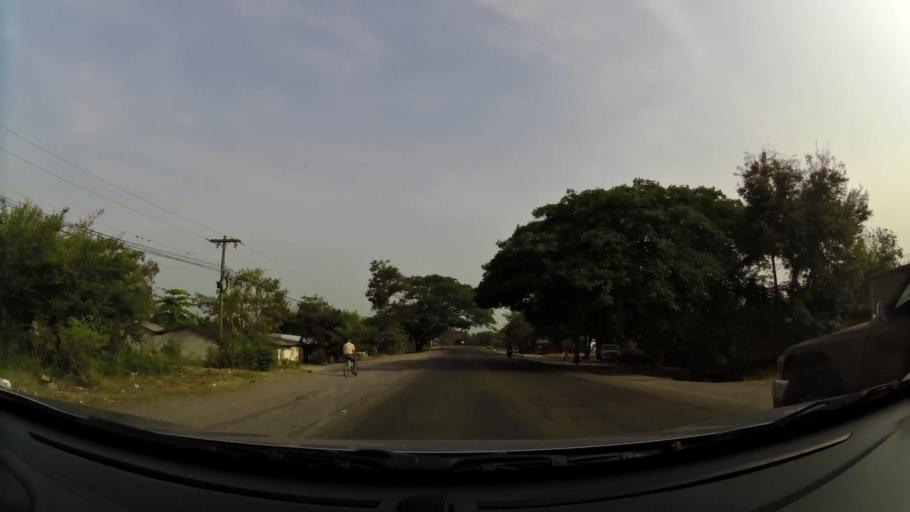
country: HN
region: Comayagua
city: Flores
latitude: 14.2887
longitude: -87.5698
